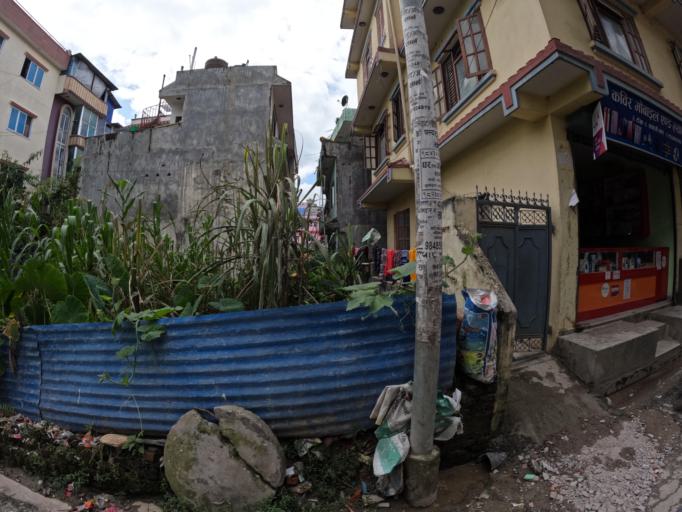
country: NP
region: Central Region
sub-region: Bagmati Zone
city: Kathmandu
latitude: 27.7480
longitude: 85.3155
